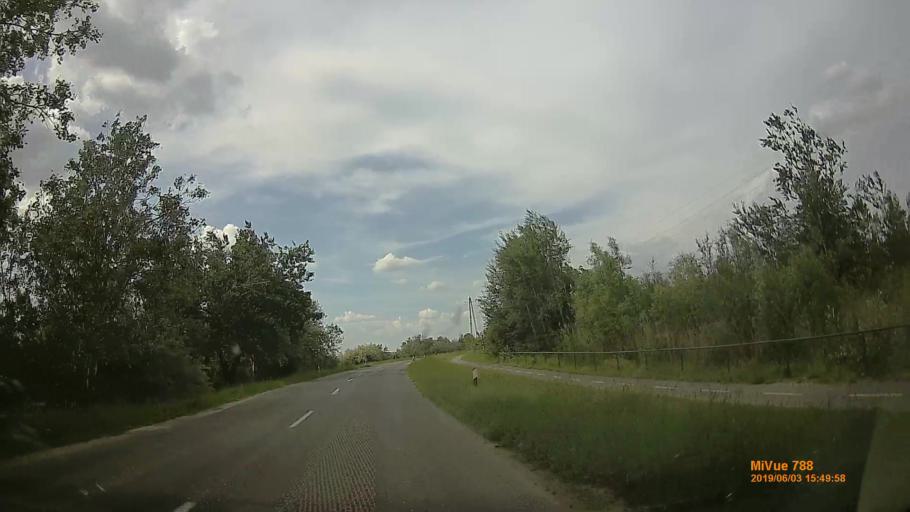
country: HU
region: Bacs-Kiskun
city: Akaszto
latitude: 46.7035
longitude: 19.1889
